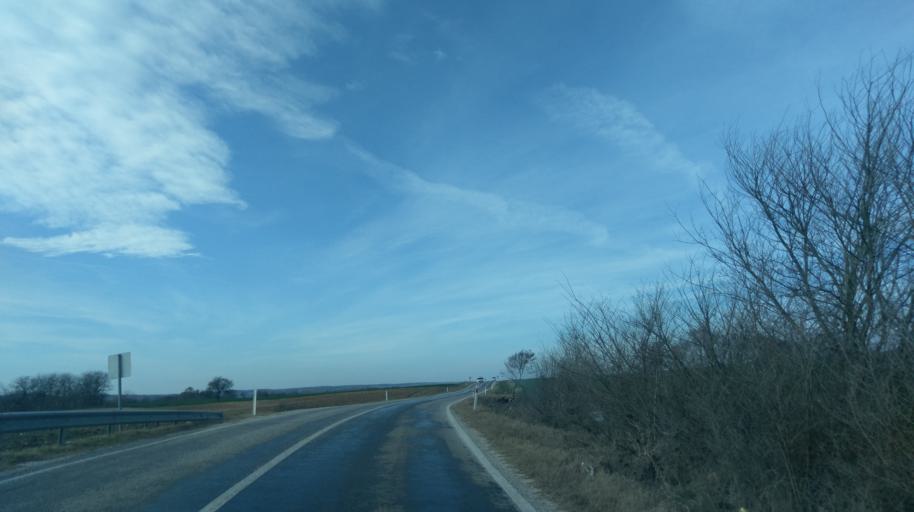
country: TR
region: Kirklareli
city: Pehlivankoy
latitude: 41.3708
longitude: 26.9873
